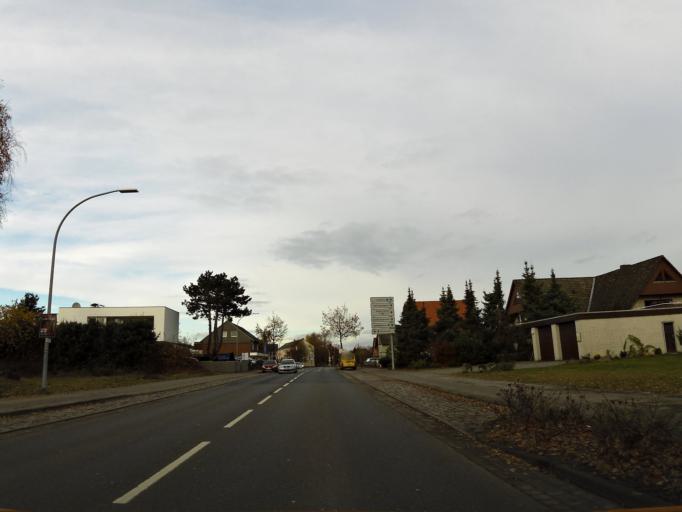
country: DE
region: Lower Saxony
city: Munster
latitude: 52.9839
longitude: 10.0869
